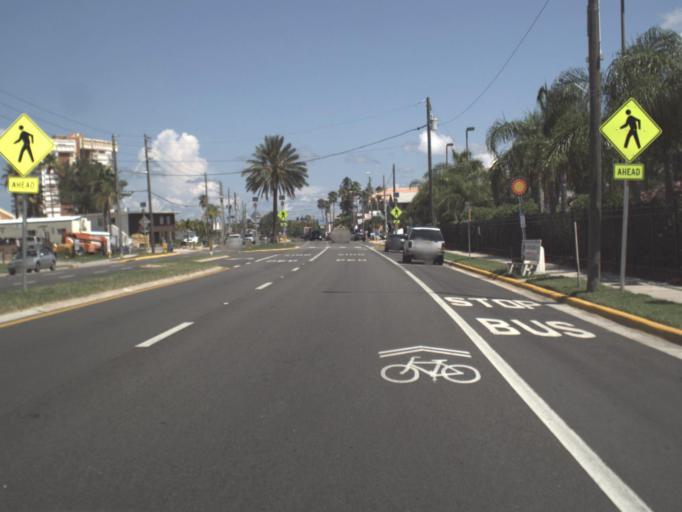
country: US
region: Florida
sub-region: Pinellas County
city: Redington Shores
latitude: 27.8262
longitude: -82.8291
